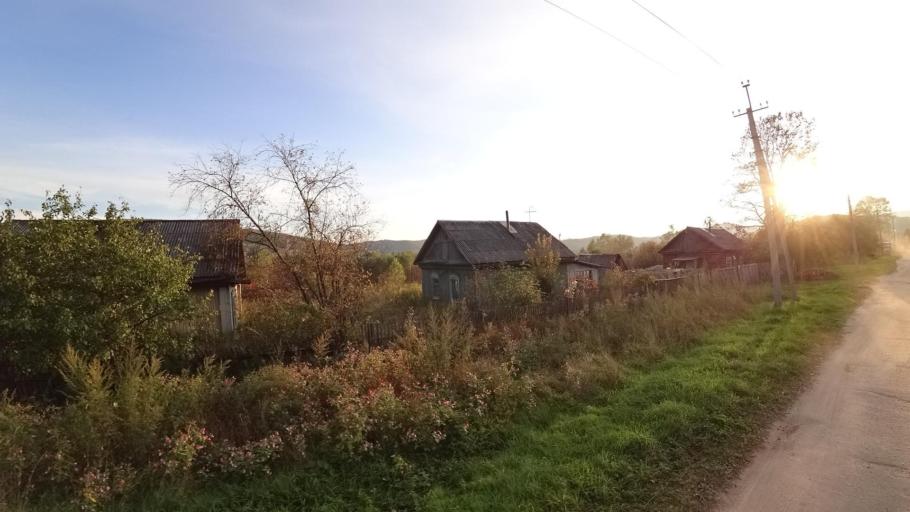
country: RU
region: Jewish Autonomous Oblast
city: Kul'dur
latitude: 49.2079
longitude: 131.6433
